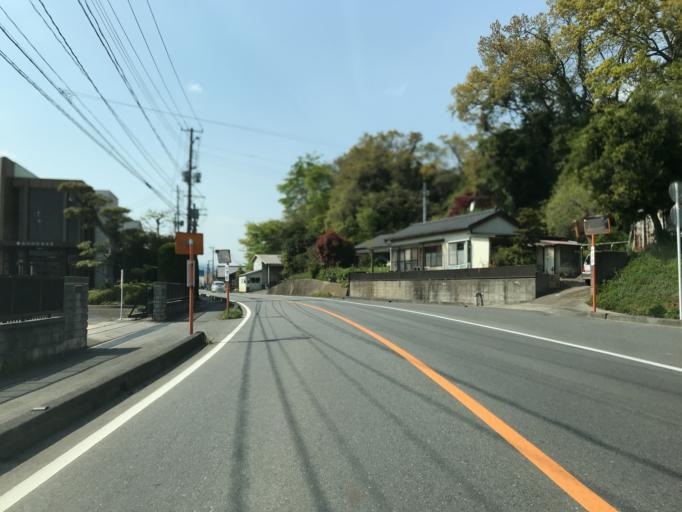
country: JP
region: Ibaraki
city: Kitaibaraki
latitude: 36.9186
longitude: 140.7901
